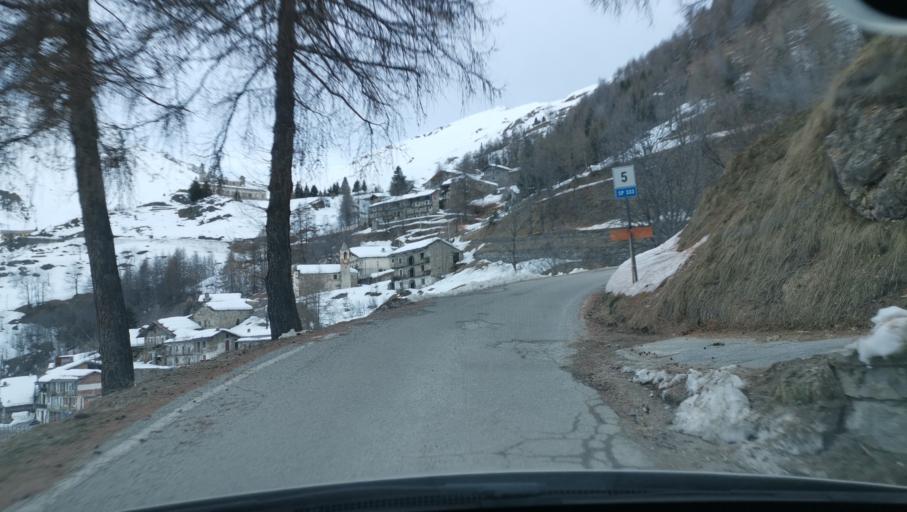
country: IT
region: Piedmont
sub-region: Provincia di Cuneo
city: Campomolino
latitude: 44.3985
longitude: 7.1776
